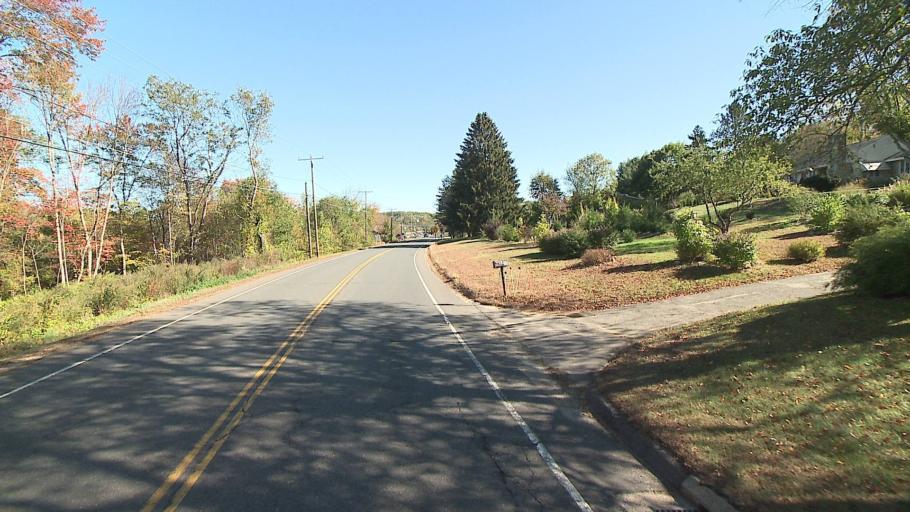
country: US
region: Connecticut
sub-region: Tolland County
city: South Coventry
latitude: 41.7172
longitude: -72.2826
